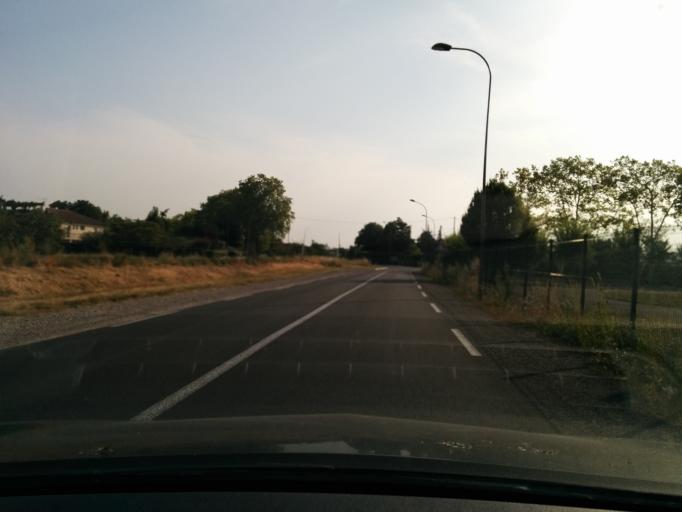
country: FR
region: Midi-Pyrenees
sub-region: Departement du Tarn
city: Gaillac
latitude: 43.9144
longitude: 1.9102
